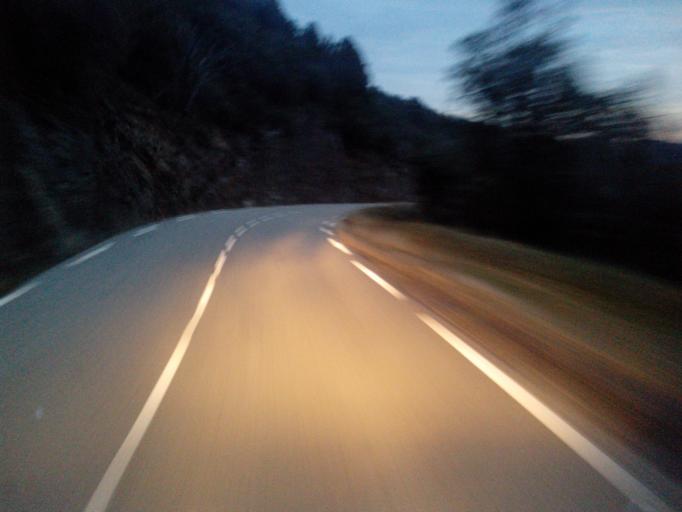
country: FR
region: Languedoc-Roussillon
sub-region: Departement du Gard
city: Saint-Jean-du-Gard
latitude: 44.1282
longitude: 3.8534
